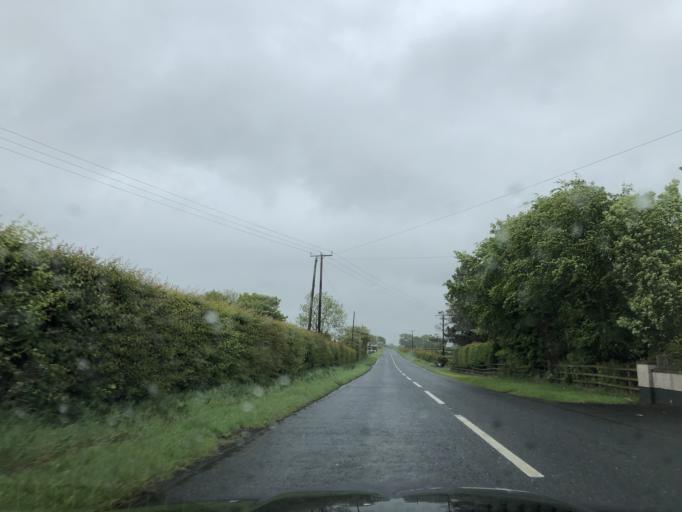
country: GB
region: Northern Ireland
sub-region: Moyle District
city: Ballycastle
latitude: 55.1820
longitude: -6.3175
